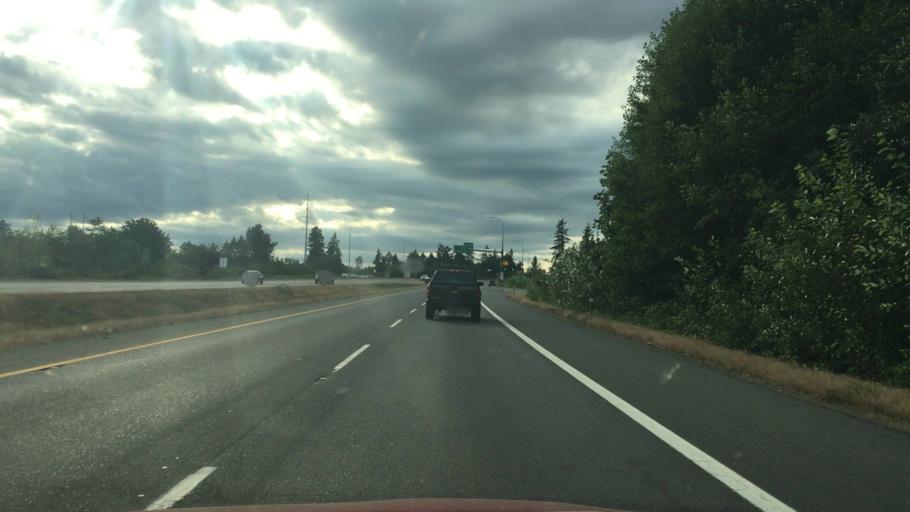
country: CA
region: British Columbia
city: Nanaimo
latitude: 49.1868
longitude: -123.9971
